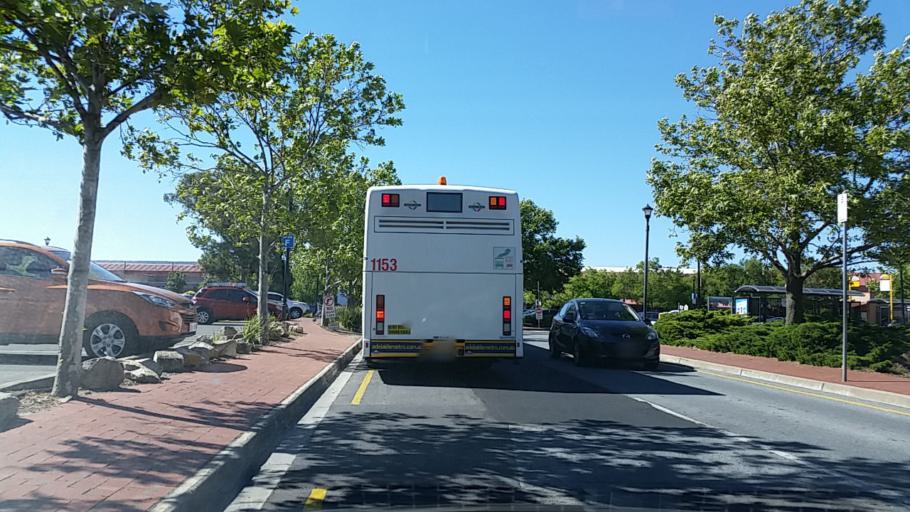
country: AU
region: South Australia
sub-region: Tea Tree Gully
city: Golden Grove
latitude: -34.7914
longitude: 138.6933
